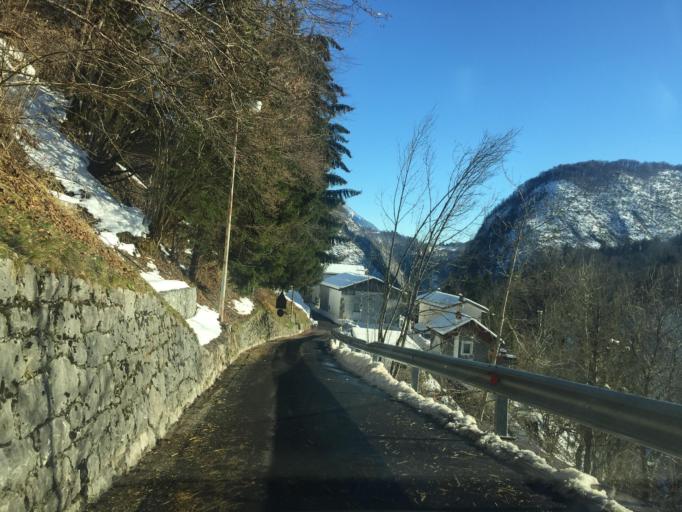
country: IT
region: Friuli Venezia Giulia
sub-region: Provincia di Udine
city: Lauco
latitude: 46.4409
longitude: 12.9447
